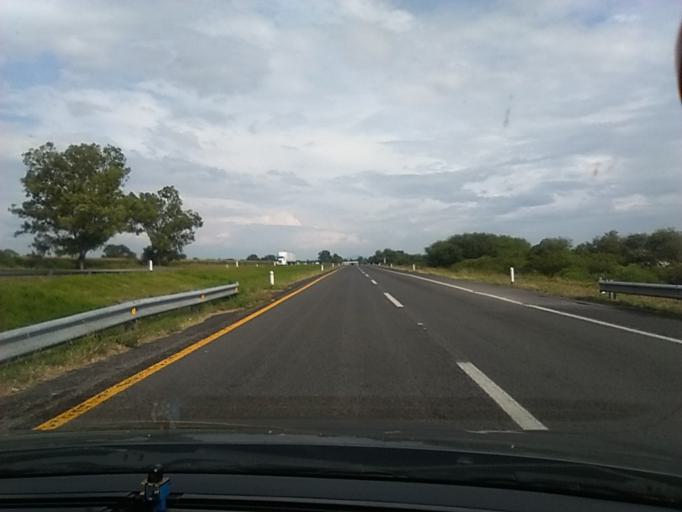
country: MX
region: Jalisco
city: La Barca
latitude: 20.3404
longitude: -102.6086
